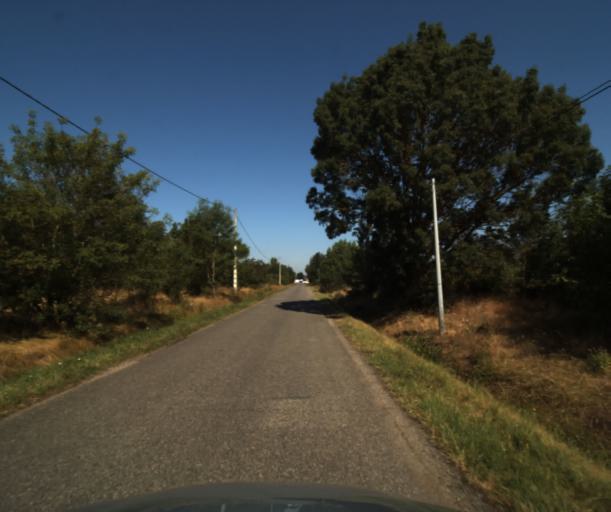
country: FR
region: Midi-Pyrenees
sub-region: Departement de la Haute-Garonne
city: Labastidette
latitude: 43.4578
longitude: 1.2545
